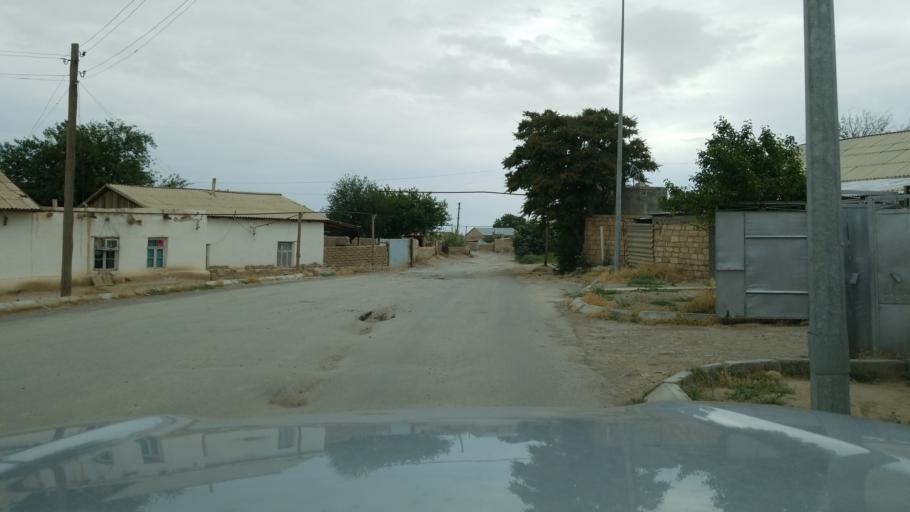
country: TM
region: Balkan
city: Serdar
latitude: 38.9867
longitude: 56.2760
